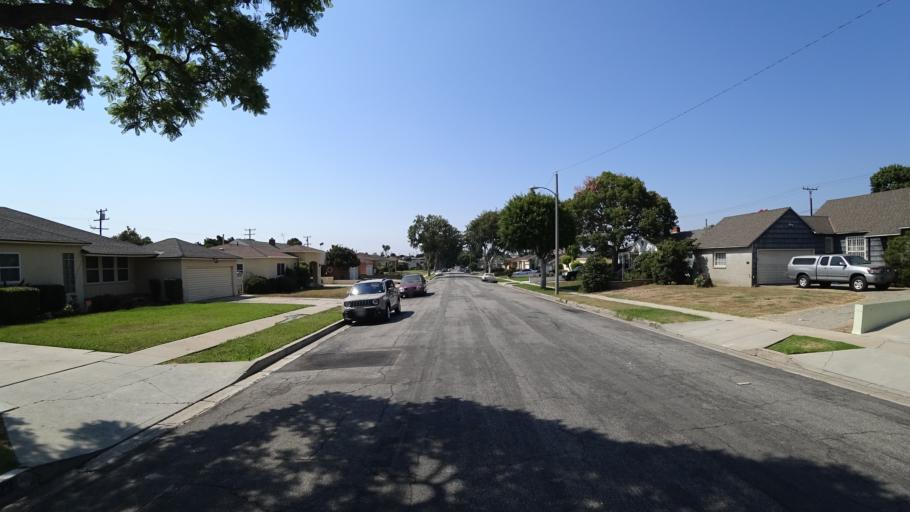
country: US
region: California
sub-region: Los Angeles County
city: Westmont
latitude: 33.9481
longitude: -118.3189
